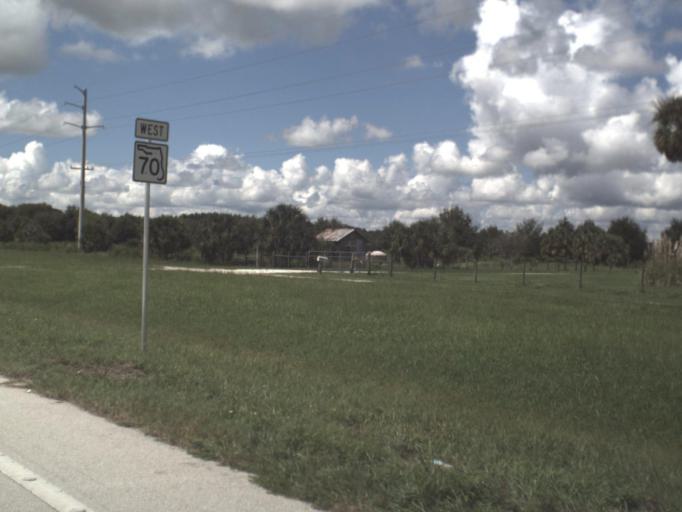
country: US
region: Florida
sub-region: DeSoto County
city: Southeast Arcadia
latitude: 27.2088
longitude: -81.7524
